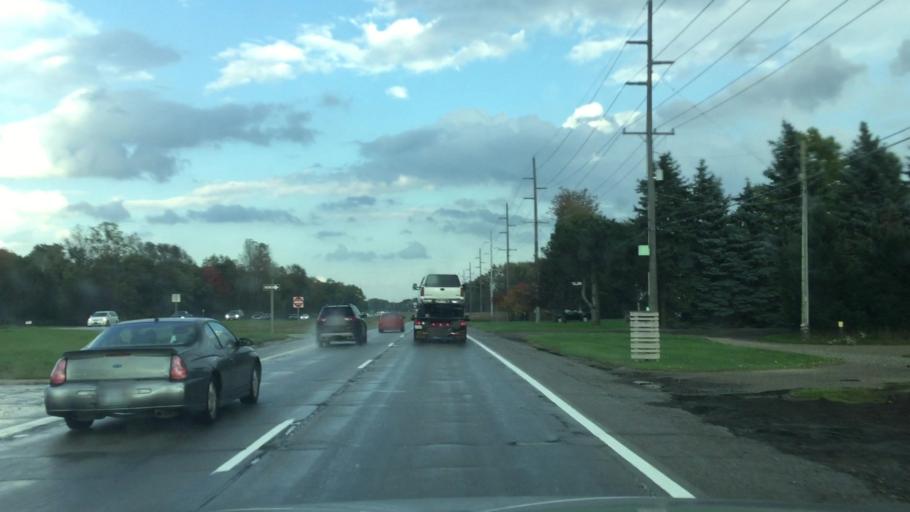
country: US
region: Michigan
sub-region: Oakland County
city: Milford
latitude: 42.6365
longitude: -83.6503
